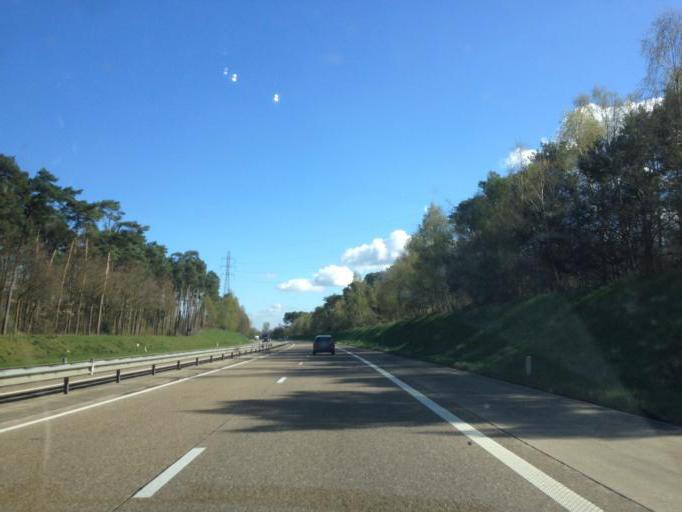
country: BE
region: Flanders
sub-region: Provincie Limburg
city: Peer
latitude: 51.1434
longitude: 5.4009
